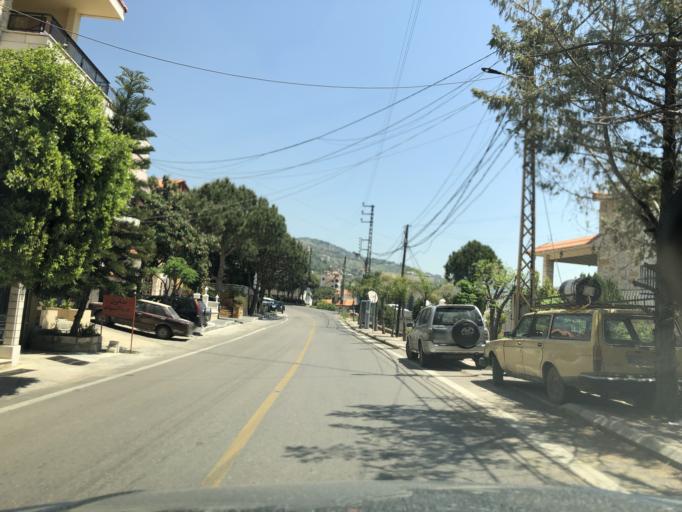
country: LB
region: Mont-Liban
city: Beit ed Dine
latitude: 33.6885
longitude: 35.5270
